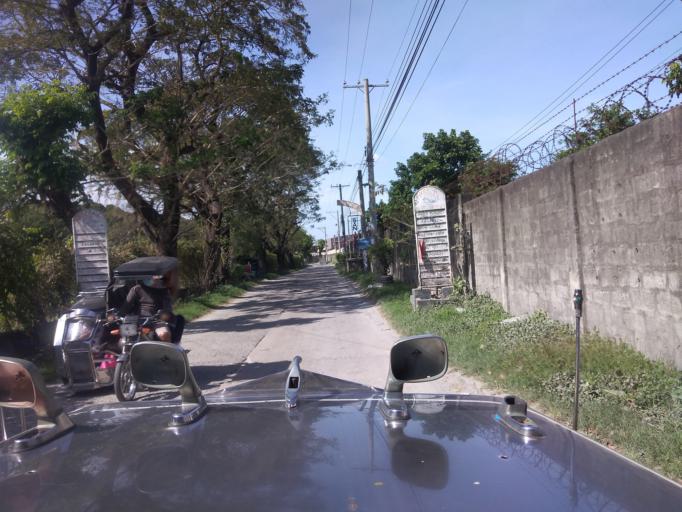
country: PH
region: Central Luzon
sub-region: Province of Pampanga
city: Magliman
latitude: 15.0390
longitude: 120.6604
